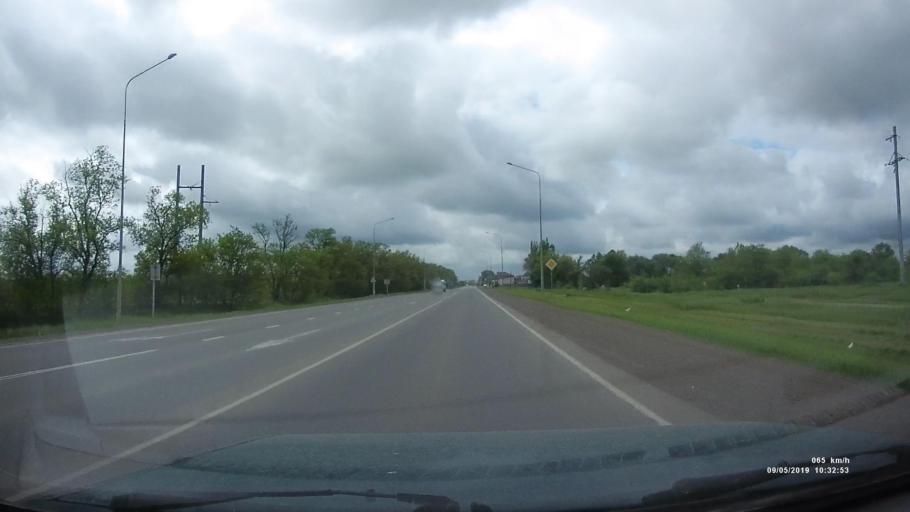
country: RU
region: Rostov
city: Azov
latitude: 47.0683
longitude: 39.4256
